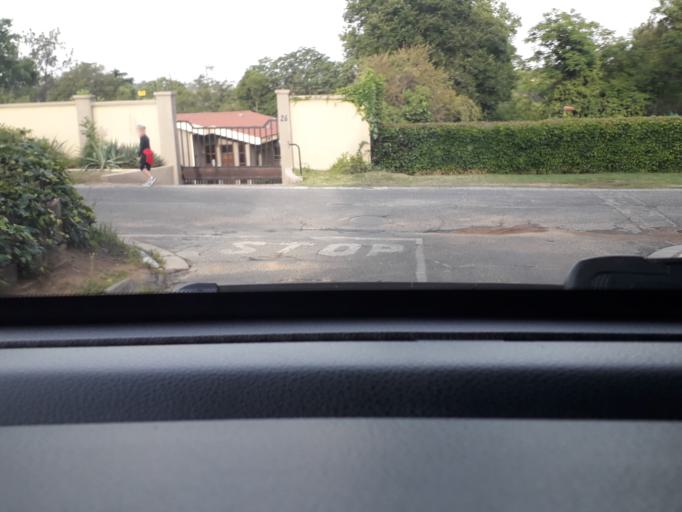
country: ZA
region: Gauteng
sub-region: City of Johannesburg Metropolitan Municipality
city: Midrand
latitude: -26.0639
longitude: 28.0635
